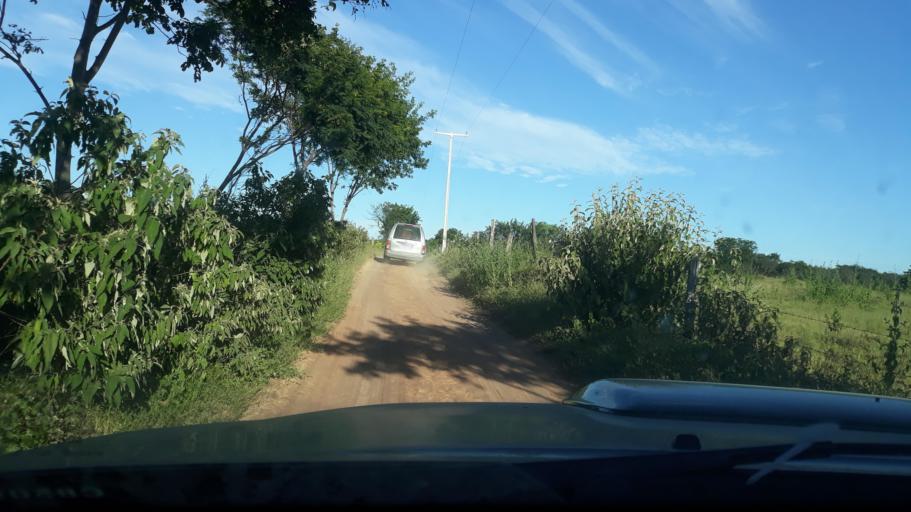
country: BR
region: Bahia
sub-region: Riacho De Santana
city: Riacho de Santana
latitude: -13.8636
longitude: -43.0214
